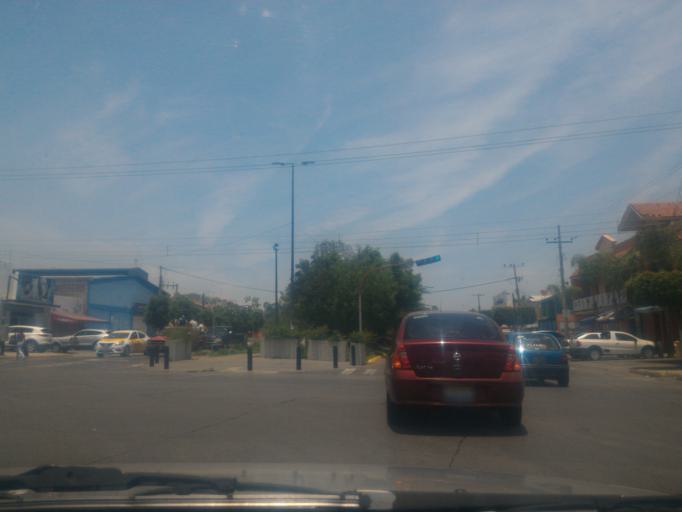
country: MX
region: Jalisco
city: Guadalajara
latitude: 20.6218
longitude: -103.3631
